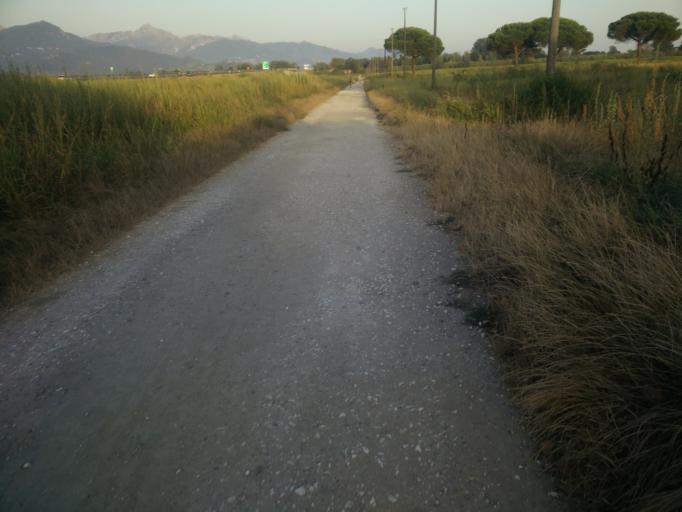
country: IT
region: Liguria
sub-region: Provincia di La Spezia
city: Casano-Dogana-Isola
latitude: 44.0565
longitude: 10.0180
